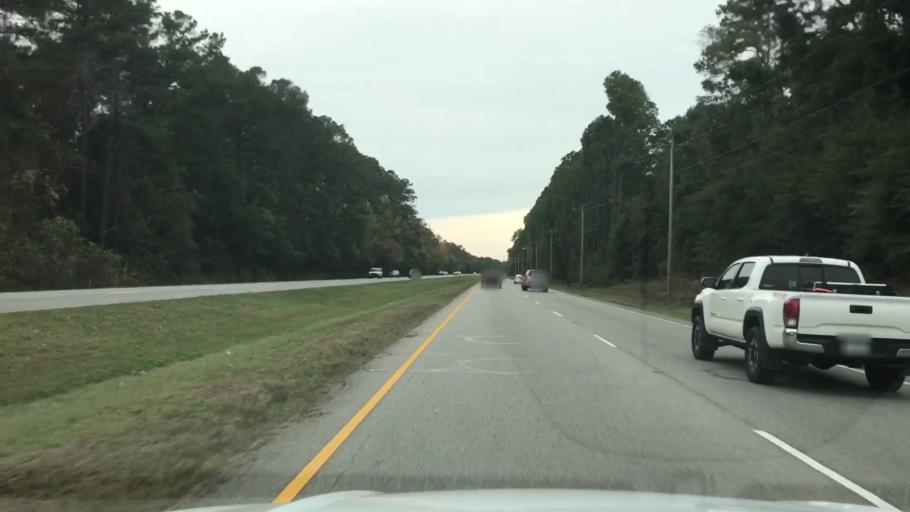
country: US
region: South Carolina
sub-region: Georgetown County
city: Georgetown
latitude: 33.3645
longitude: -79.2299
